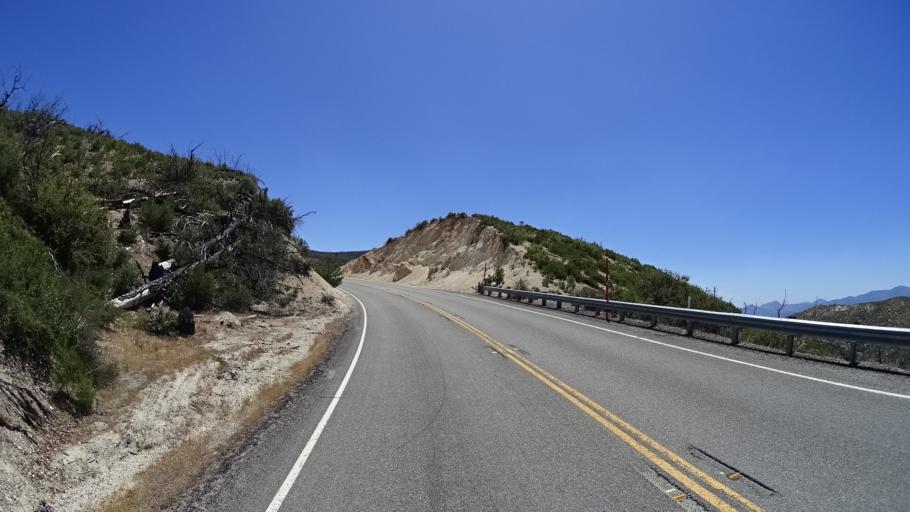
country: US
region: California
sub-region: Los Angeles County
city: Sierra Madre
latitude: 34.3097
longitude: -118.0158
